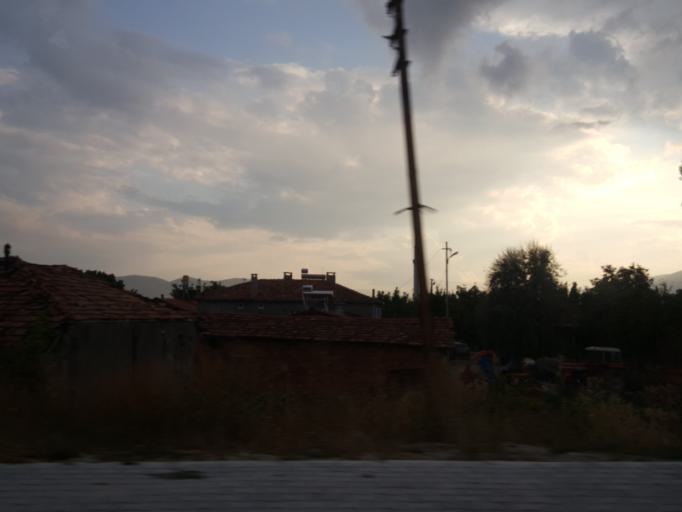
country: TR
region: Amasya
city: Gumushacikoy
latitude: 40.8799
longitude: 35.2236
